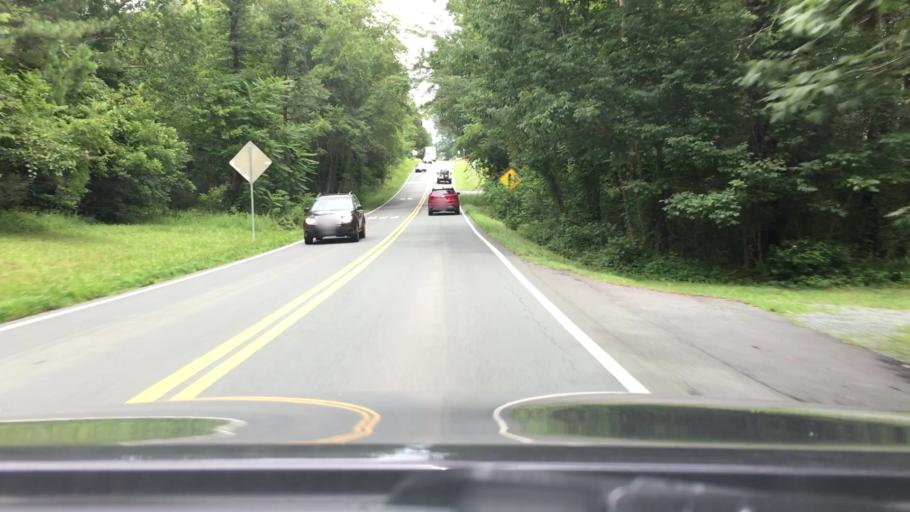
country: US
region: Virginia
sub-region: Fluvanna County
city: Lake Monticello
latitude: 38.0238
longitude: -78.3571
